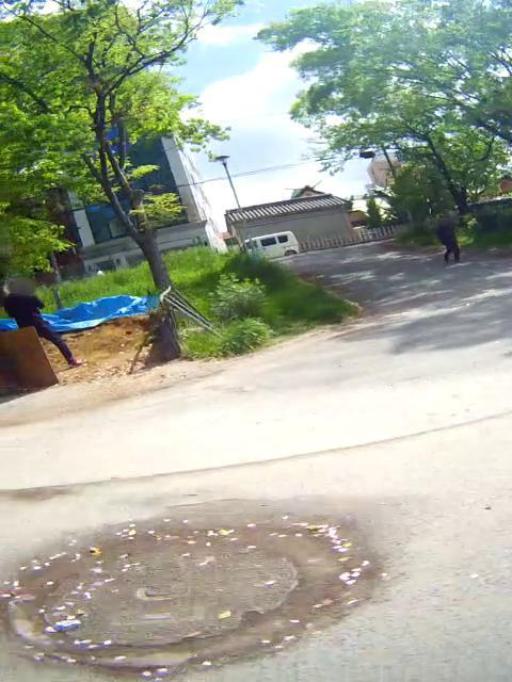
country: JP
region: Osaka
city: Osaka-shi
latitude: 34.7037
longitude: 135.5203
